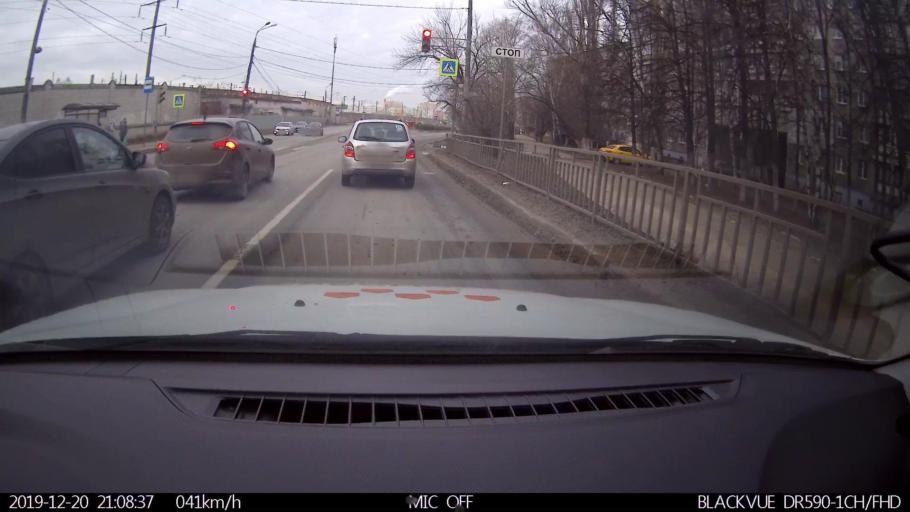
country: RU
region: Nizjnij Novgorod
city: Nizhniy Novgorod
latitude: 56.3363
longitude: 43.9279
